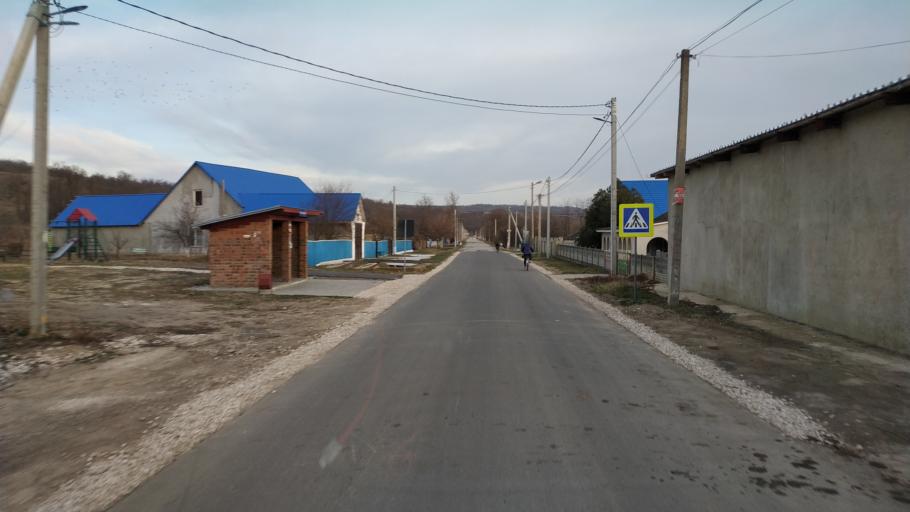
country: MD
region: Hincesti
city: Dancu
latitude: 46.7885
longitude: 28.1892
